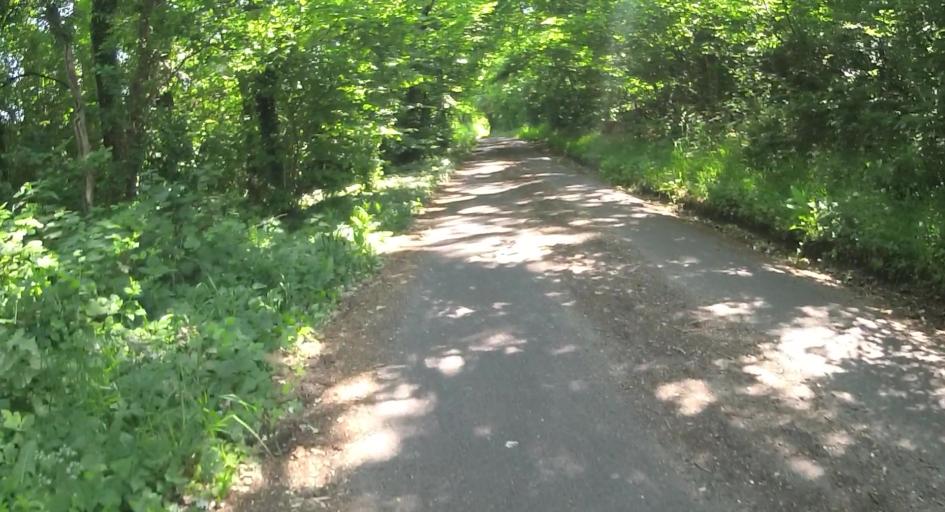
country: GB
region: England
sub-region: West Berkshire
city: Greenham
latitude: 51.3621
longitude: -1.2771
